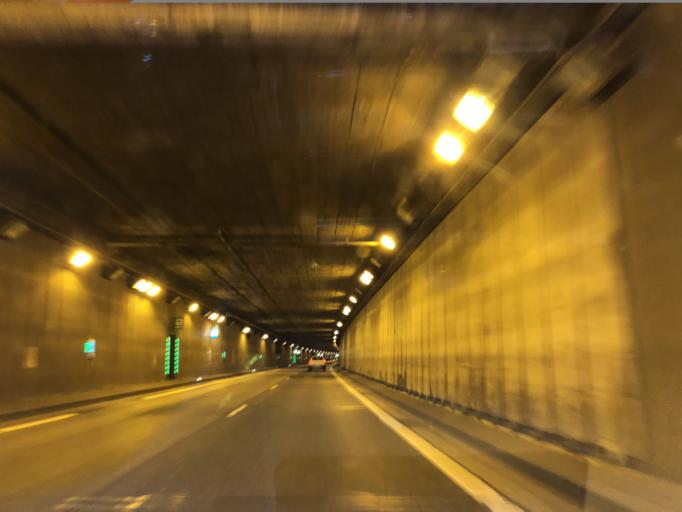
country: DE
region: North Rhine-Westphalia
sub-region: Regierungsbezirk Dusseldorf
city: Dusseldorf
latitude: 51.2272
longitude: 6.7476
